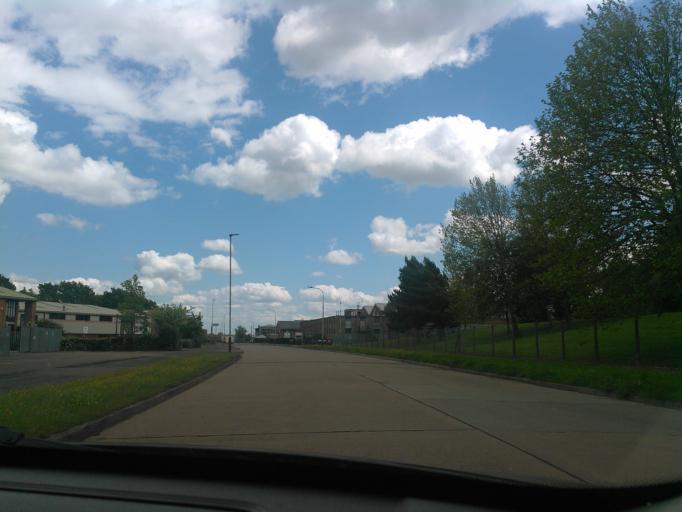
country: GB
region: England
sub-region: Leicestershire
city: Glenfield
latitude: 52.6348
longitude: -1.2032
